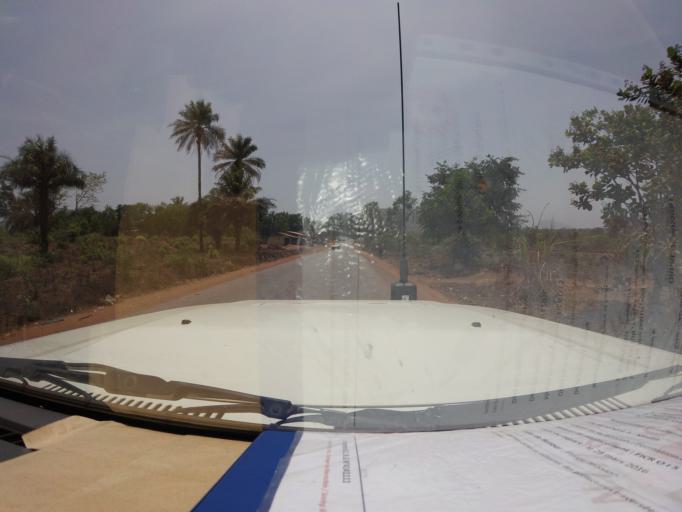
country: GN
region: Kindia
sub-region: Coyah
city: Coyah
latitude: 9.7898
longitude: -13.3071
